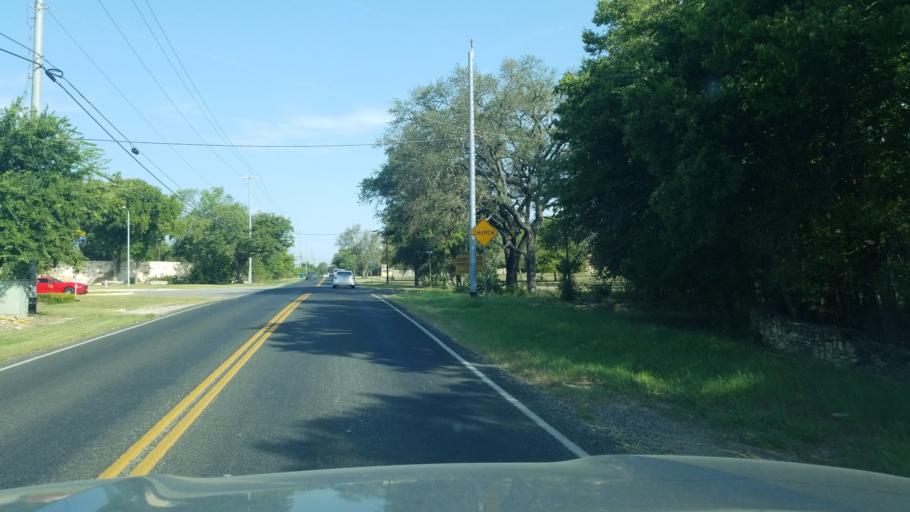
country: US
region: Texas
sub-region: Bexar County
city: Helotes
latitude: 29.4638
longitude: -98.7621
